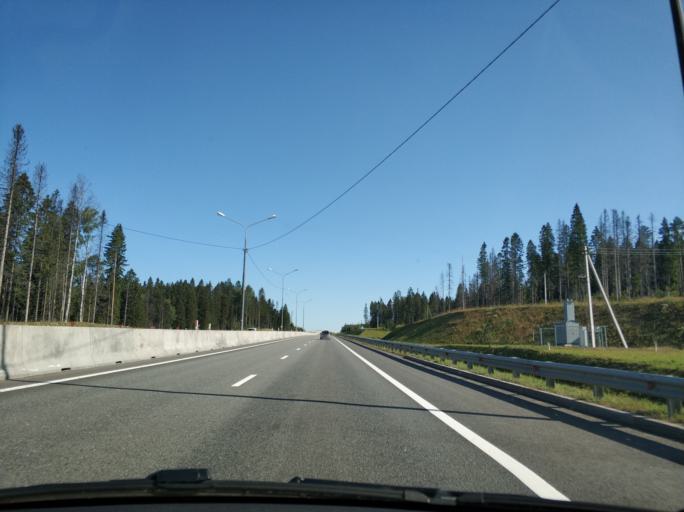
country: RU
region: Leningrad
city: Sosnovo
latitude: 60.4609
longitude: 30.1962
